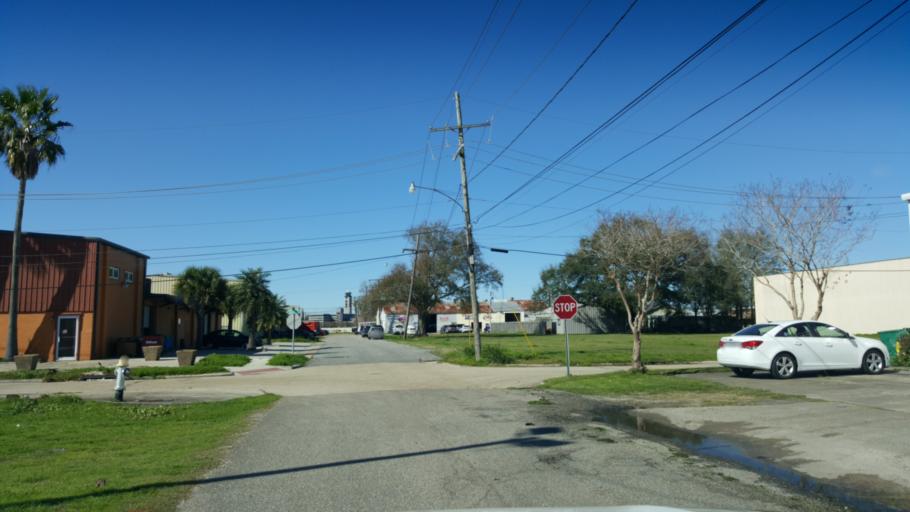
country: US
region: Louisiana
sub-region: Jefferson Parish
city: Kenner
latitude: 29.9814
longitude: -90.2475
